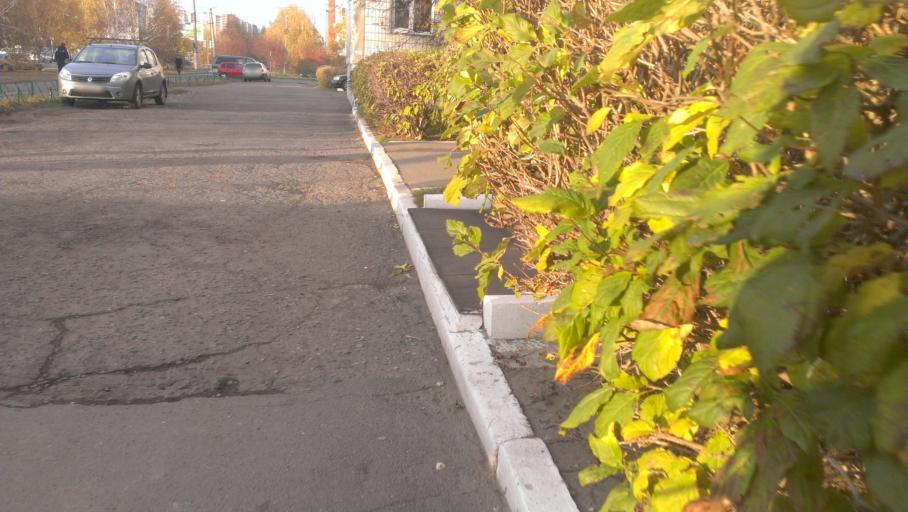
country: RU
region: Altai Krai
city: Novosilikatnyy
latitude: 53.3385
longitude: 83.6703
